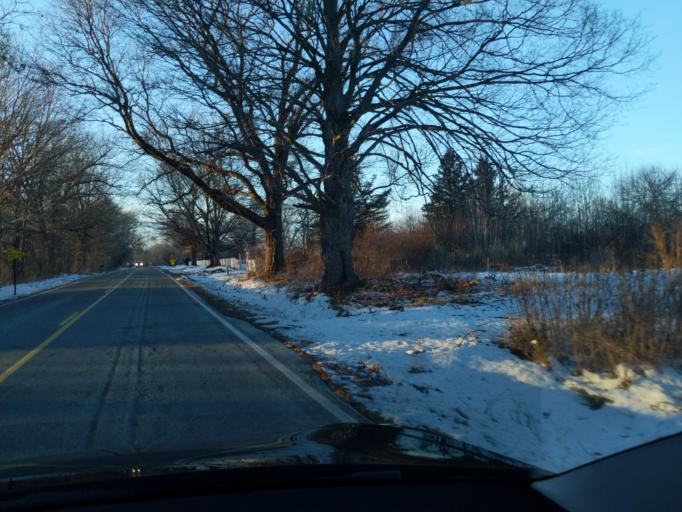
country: US
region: Michigan
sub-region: Ingham County
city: Stockbridge
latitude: 42.5106
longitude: -84.2637
